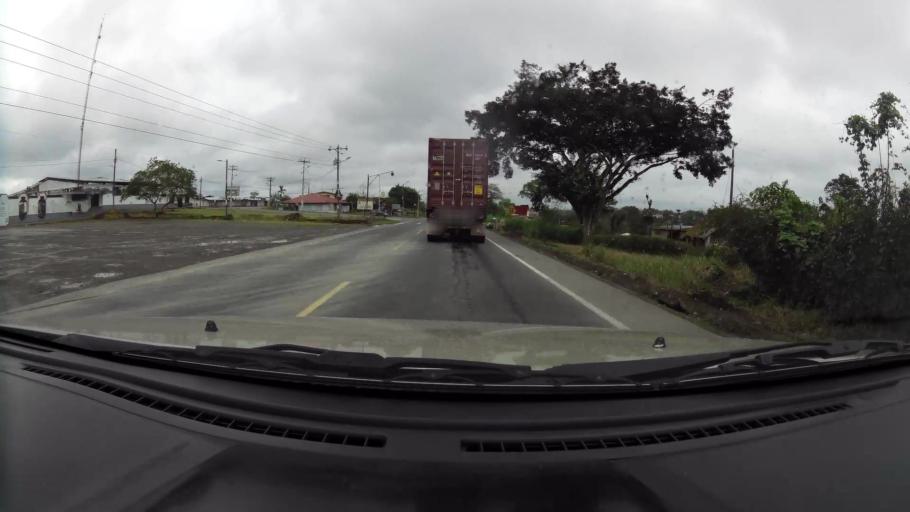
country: EC
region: Santo Domingo de los Tsachilas
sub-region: Canton Santo Domingo de los Colorados
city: Santo Domingo de los Colorados
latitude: -0.2731
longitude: -79.1592
